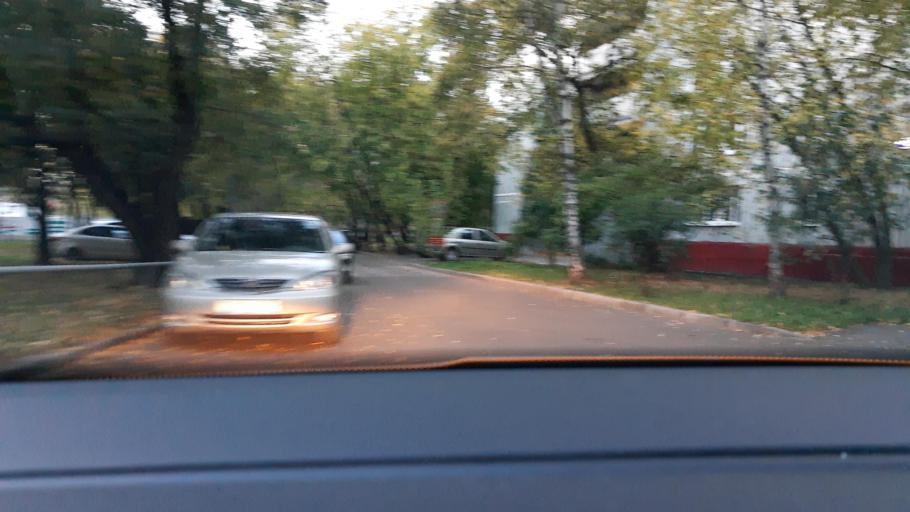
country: RU
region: Moscow
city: Leonovo
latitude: 55.8796
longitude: 37.6488
